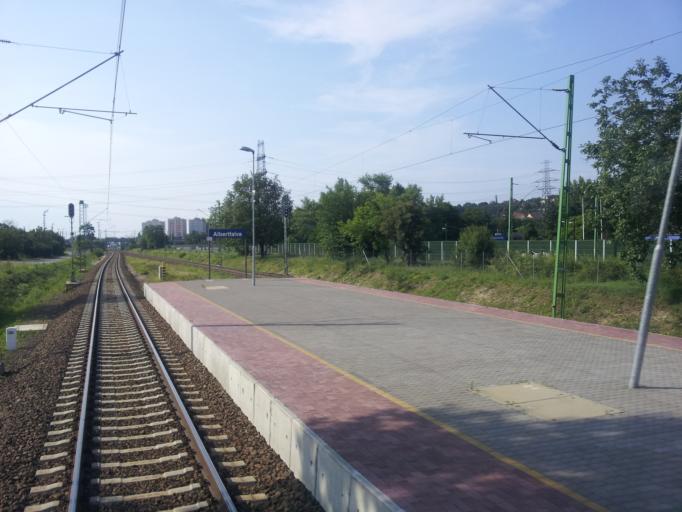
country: HU
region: Budapest
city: Budapest XXII. keruelet
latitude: 47.4405
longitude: 19.0344
